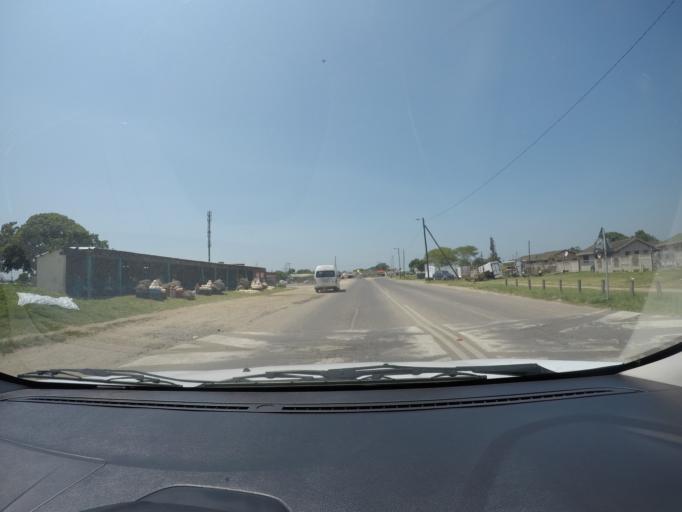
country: ZA
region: KwaZulu-Natal
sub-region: uThungulu District Municipality
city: eSikhawini
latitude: -28.8685
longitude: 31.9268
